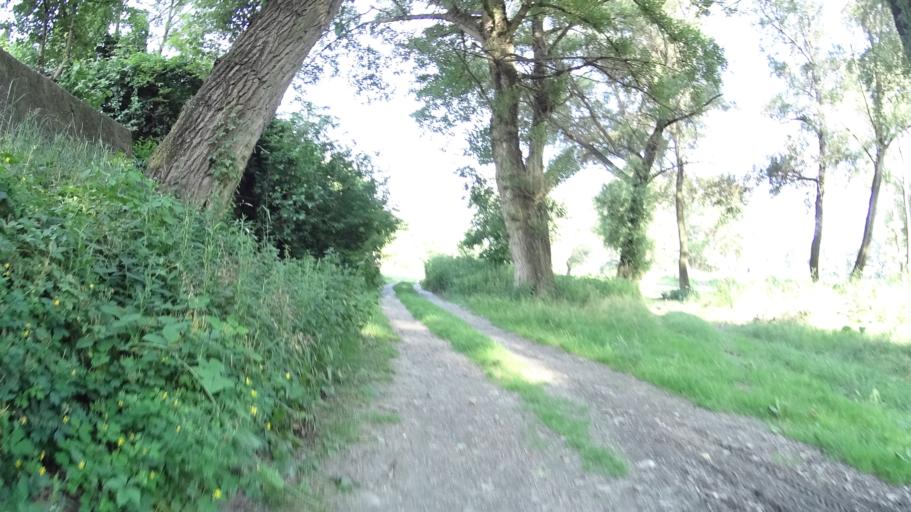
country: HU
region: Pest
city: Kismaros
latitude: 47.8071
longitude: 19.0049
